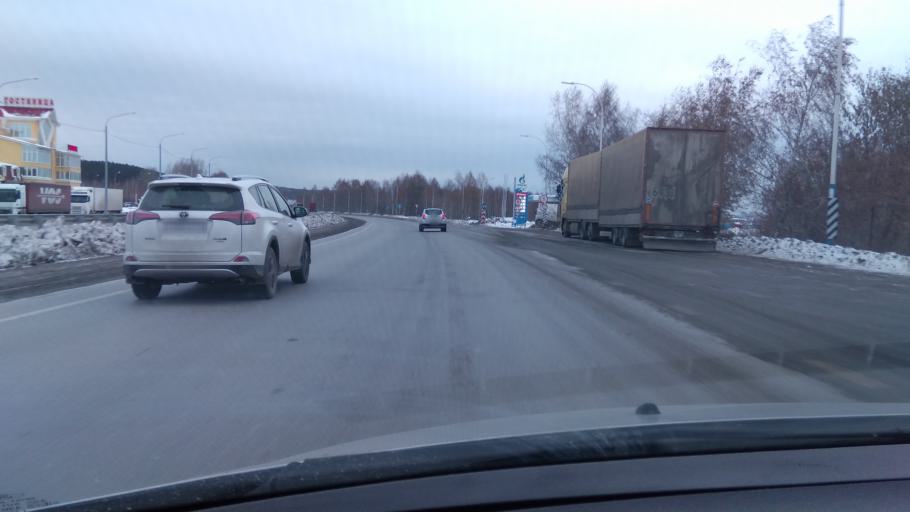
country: RU
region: Sverdlovsk
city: Aramil
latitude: 56.7049
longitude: 60.7465
